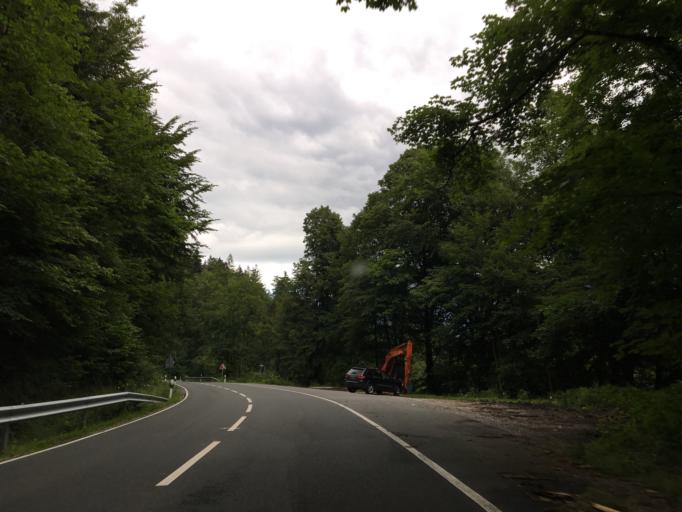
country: AT
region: Tyrol
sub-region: Politischer Bezirk Kufstein
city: Erl
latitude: 47.6878
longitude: 12.1546
